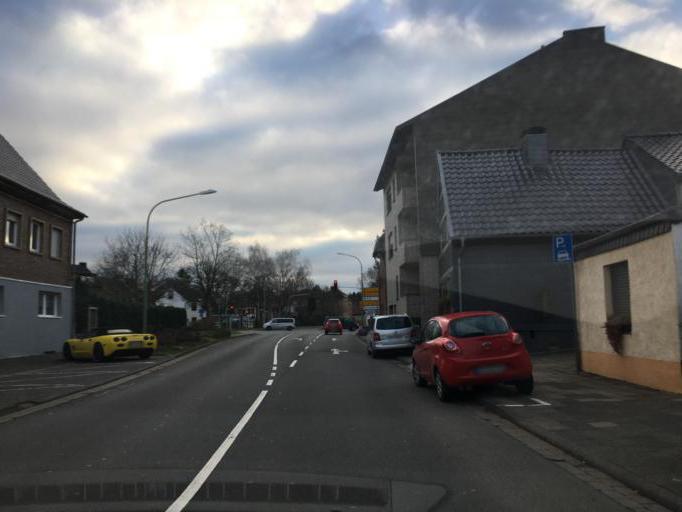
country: DE
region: North Rhine-Westphalia
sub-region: Regierungsbezirk Koln
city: Dueren
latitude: 50.7889
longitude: 6.4398
